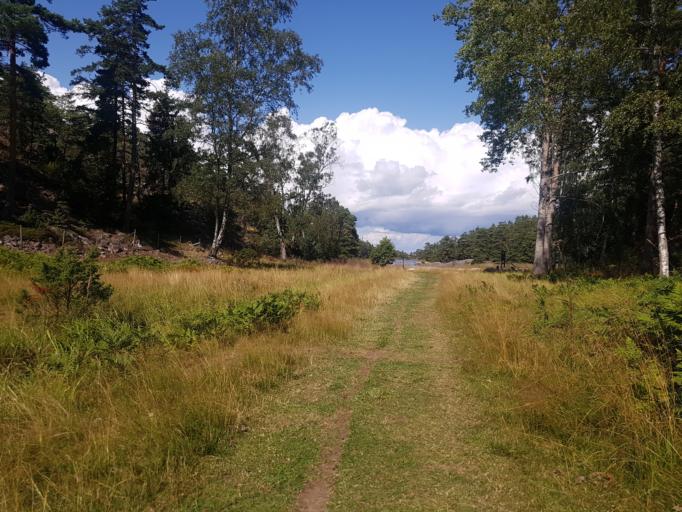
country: SE
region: Stockholm
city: Dalaro
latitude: 59.0461
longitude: 18.5209
